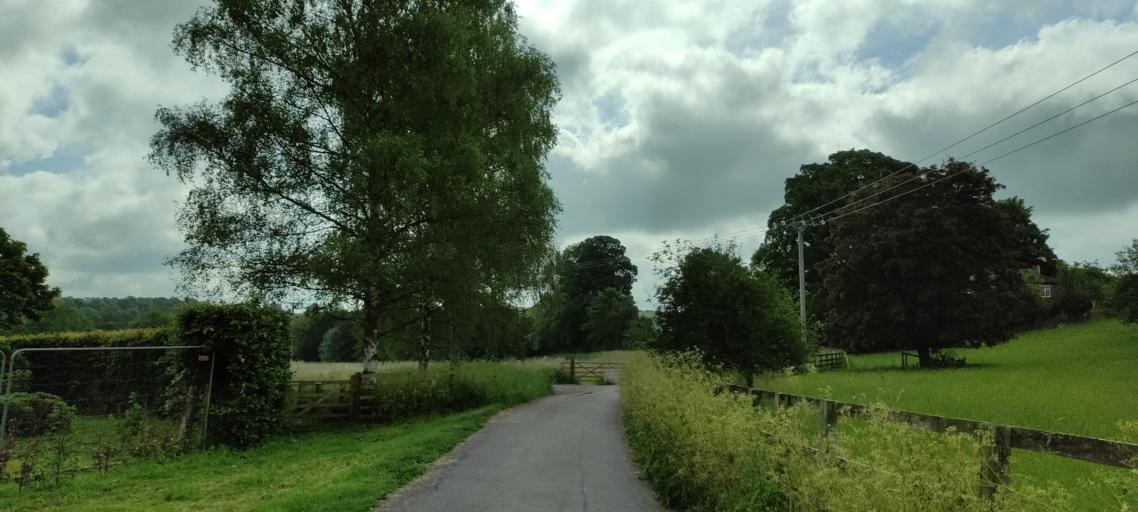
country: GB
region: England
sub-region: North Yorkshire
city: Bedale
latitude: 54.2221
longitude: -1.6519
